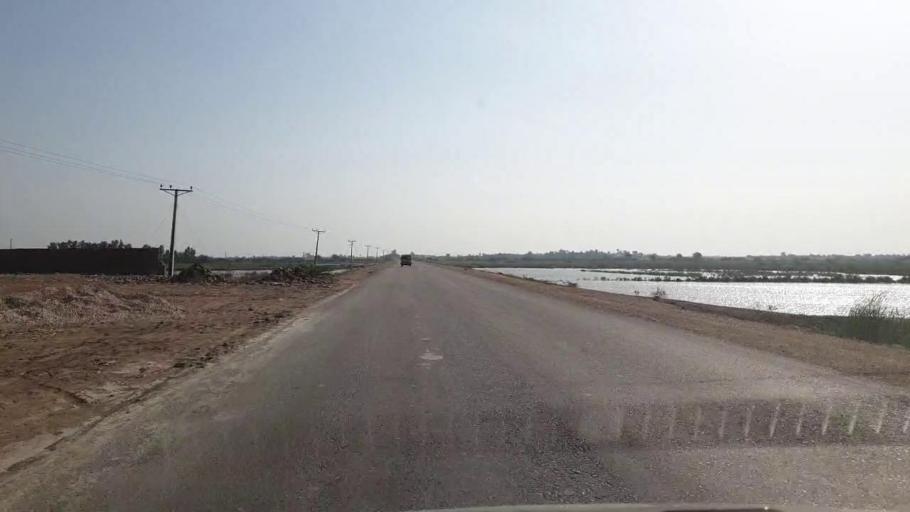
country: PK
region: Sindh
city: Badin
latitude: 24.6582
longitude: 68.9612
